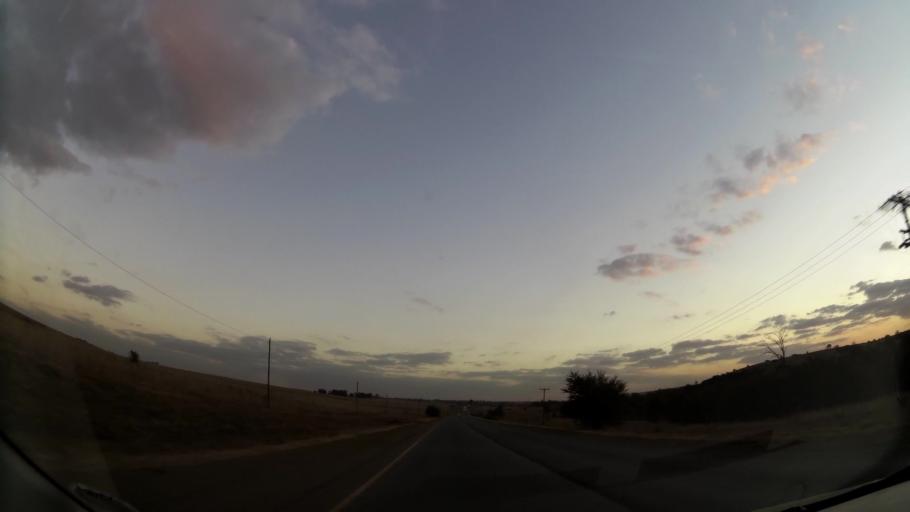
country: ZA
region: Gauteng
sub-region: West Rand District Municipality
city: Krugersdorp
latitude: -26.0498
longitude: 27.7127
